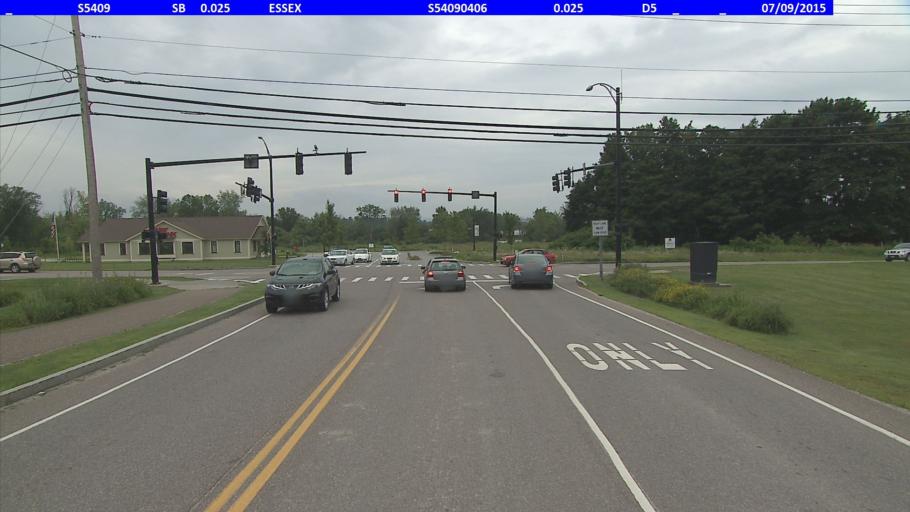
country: US
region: Vermont
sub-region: Chittenden County
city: Essex Junction
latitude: 44.5105
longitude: -73.0836
